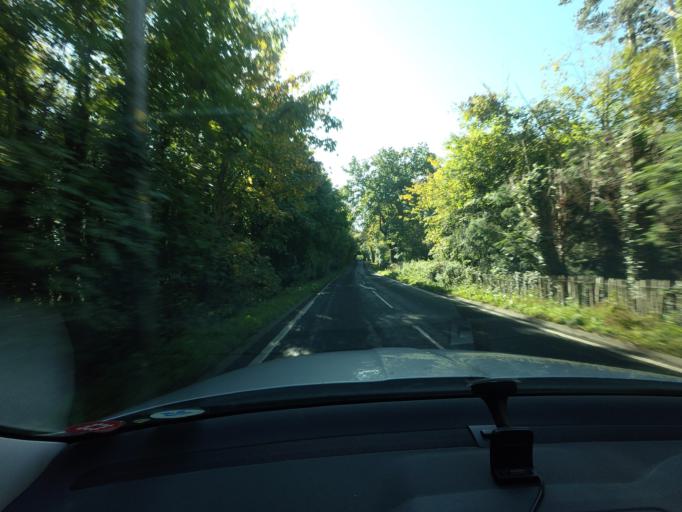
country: GB
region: England
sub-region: Kent
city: Tonbridge
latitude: 51.2350
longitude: 0.2874
